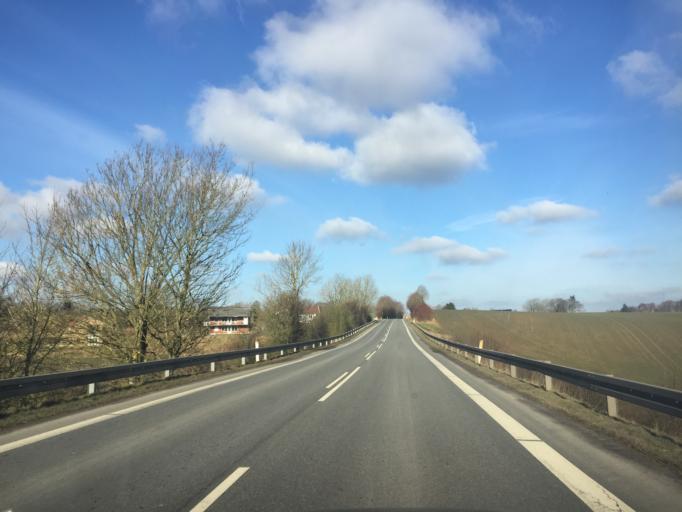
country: DK
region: South Denmark
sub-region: Assens Kommune
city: Vissenbjerg
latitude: 55.4368
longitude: 10.1834
